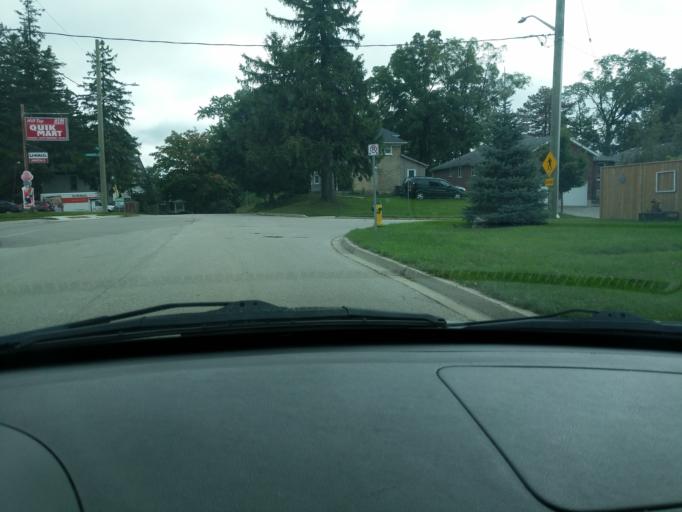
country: CA
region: Ontario
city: Cambridge
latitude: 43.4270
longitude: -80.3119
